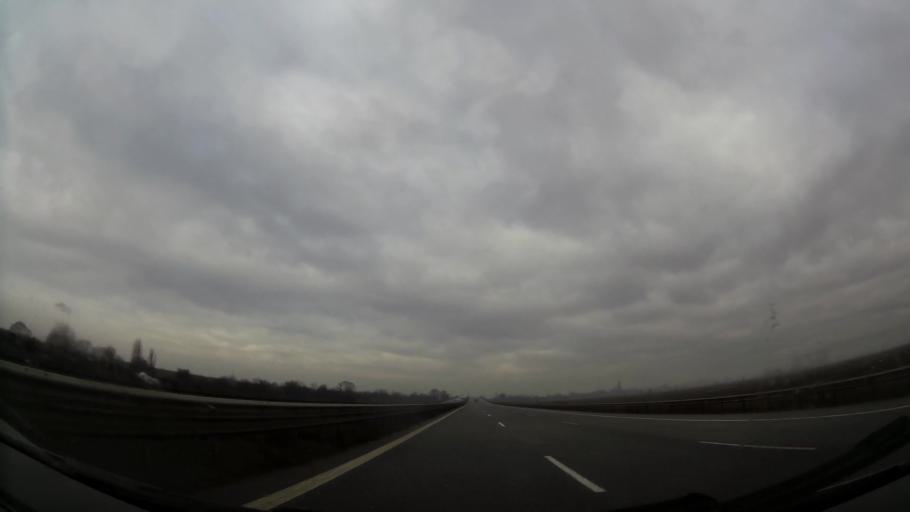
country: BG
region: Sofia-Capital
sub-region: Stolichna Obshtina
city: Sofia
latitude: 42.7352
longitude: 23.3732
